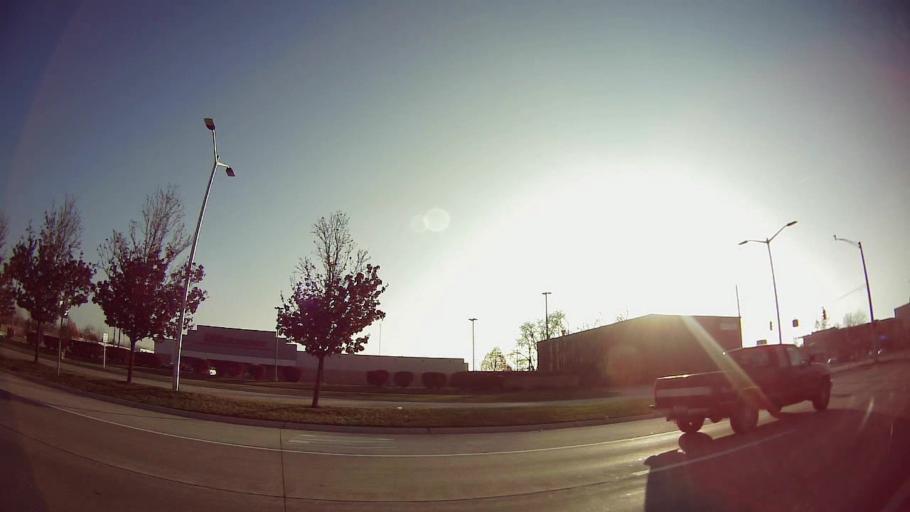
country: US
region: Michigan
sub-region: Oakland County
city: Oak Park
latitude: 42.4484
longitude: -83.2009
